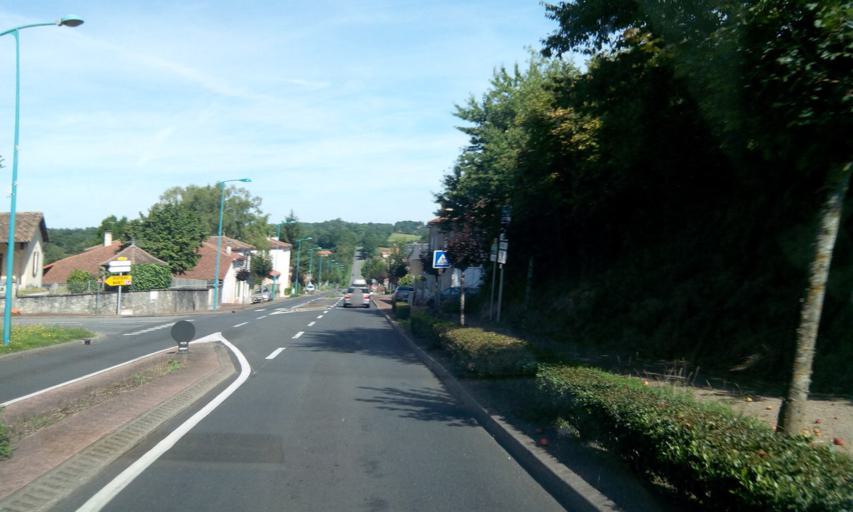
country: FR
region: Poitou-Charentes
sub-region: Departement de la Charente
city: Confolens
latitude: 45.9629
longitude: 0.7006
